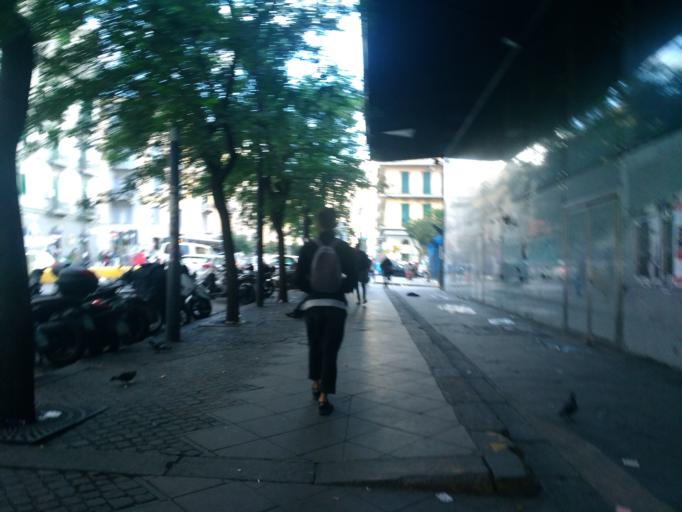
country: IT
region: Campania
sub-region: Provincia di Napoli
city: Napoli
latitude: 40.8536
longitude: 14.2717
